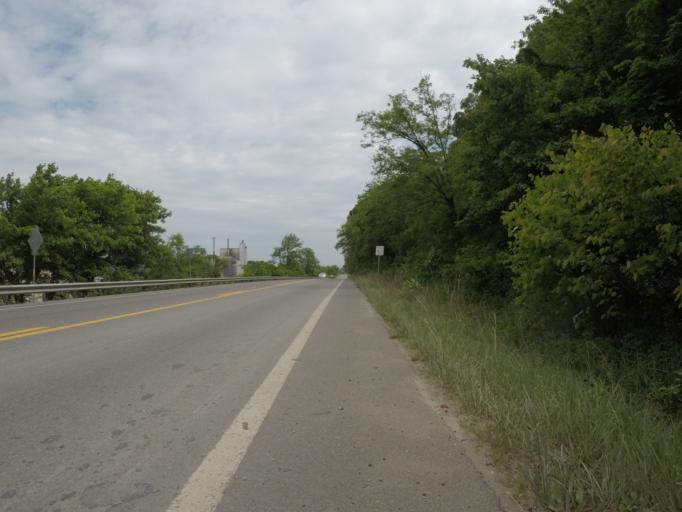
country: US
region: West Virginia
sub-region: Wayne County
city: Kenova
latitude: 38.3535
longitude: -82.5933
